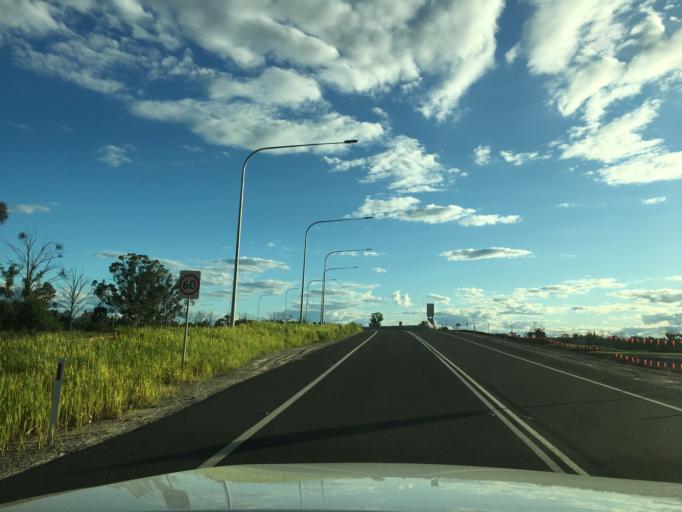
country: AU
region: New South Wales
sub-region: Liverpool
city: Bringelly
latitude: -33.8838
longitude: 150.7427
